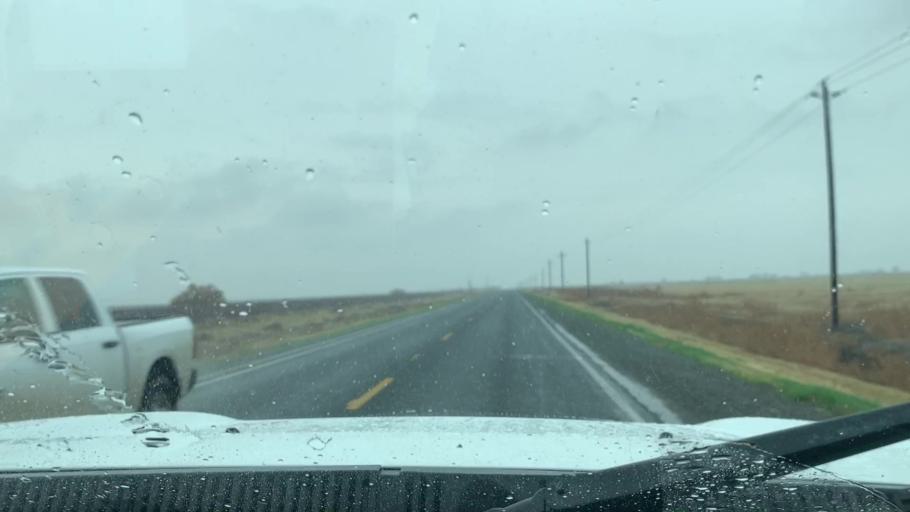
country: US
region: California
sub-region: Tulare County
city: Alpaugh
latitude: 35.8988
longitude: -119.4107
